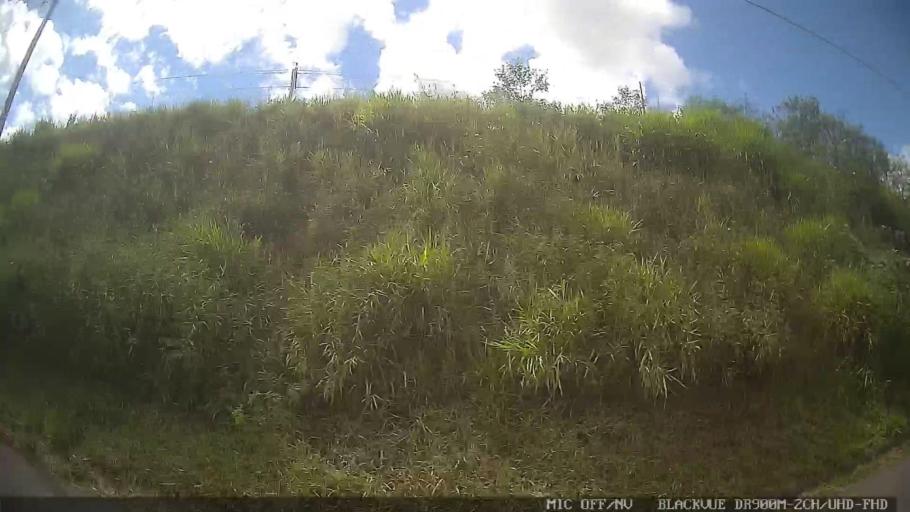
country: BR
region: Minas Gerais
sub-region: Extrema
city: Extrema
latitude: -22.8816
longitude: -46.4051
